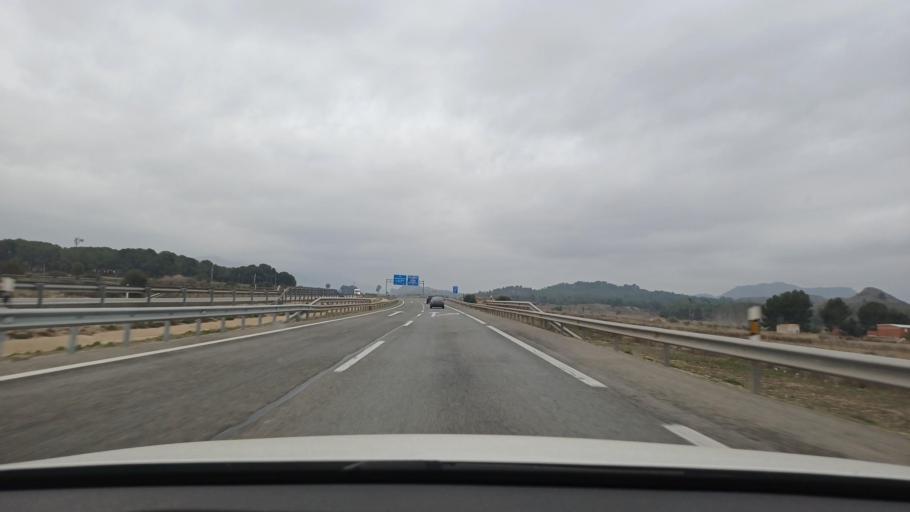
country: ES
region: Valencia
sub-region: Provincia de Alicante
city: Sax
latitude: 38.5659
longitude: -0.8346
